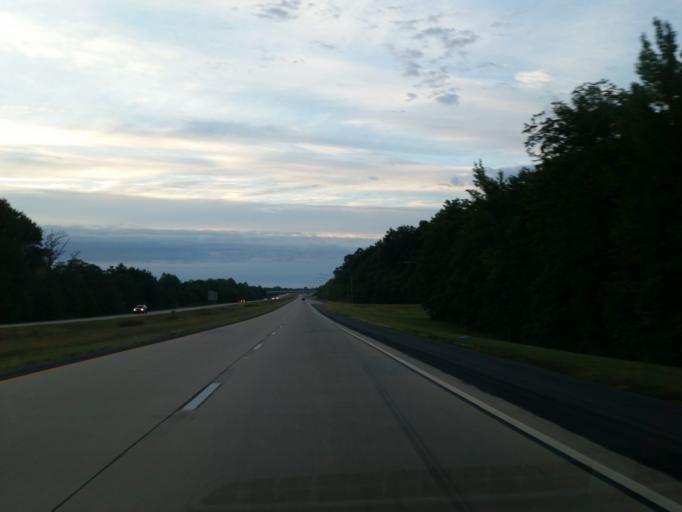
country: US
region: Delaware
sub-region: Kent County
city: Smyrna
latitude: 39.3271
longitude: -75.6194
